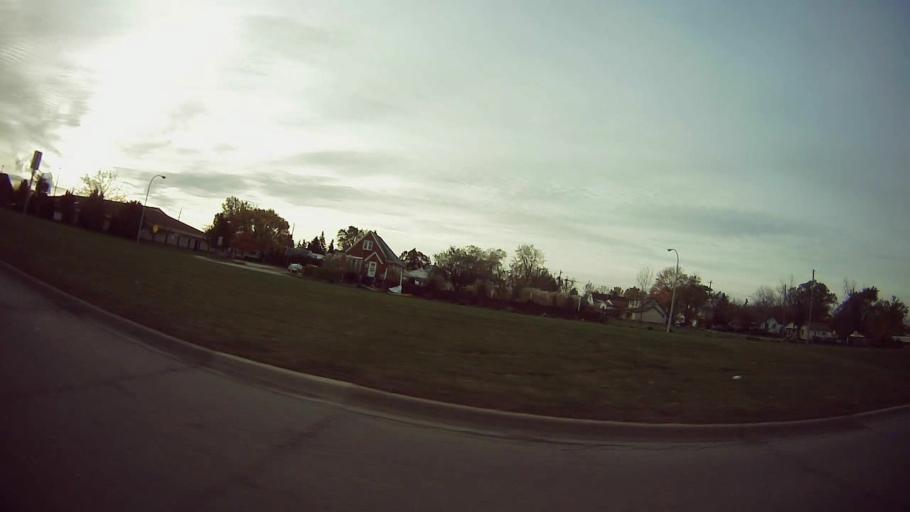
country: US
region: Michigan
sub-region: Macomb County
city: Center Line
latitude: 42.4915
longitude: -83.0492
